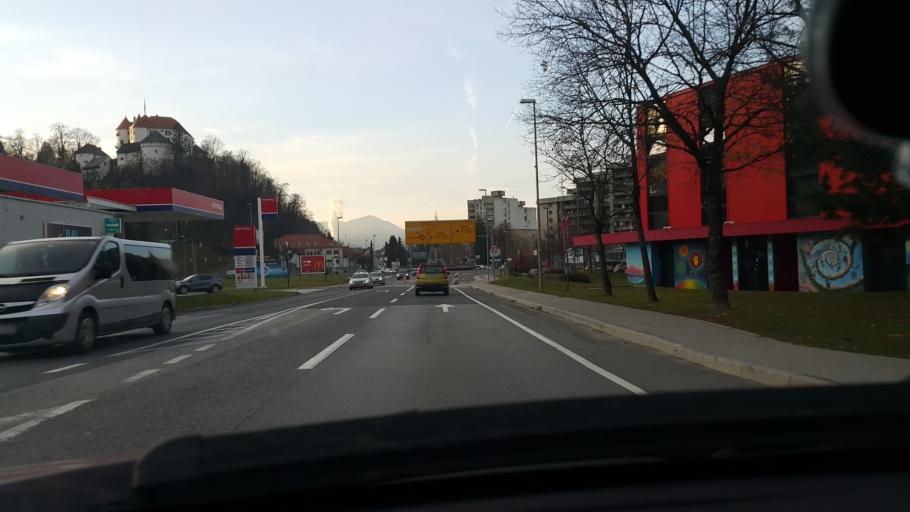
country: SI
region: Velenje
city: Velenje
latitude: 46.3563
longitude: 15.1151
